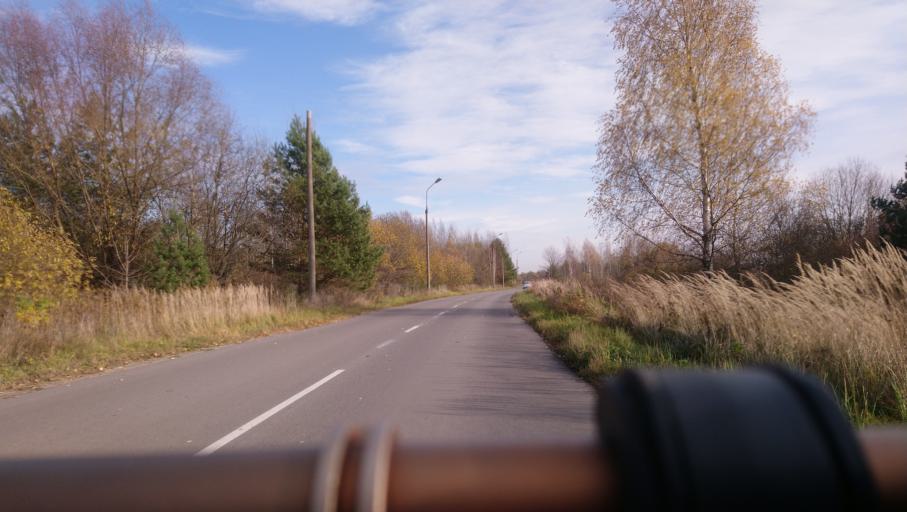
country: RU
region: Moskovskaya
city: Dubna
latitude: 56.7769
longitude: 37.2332
